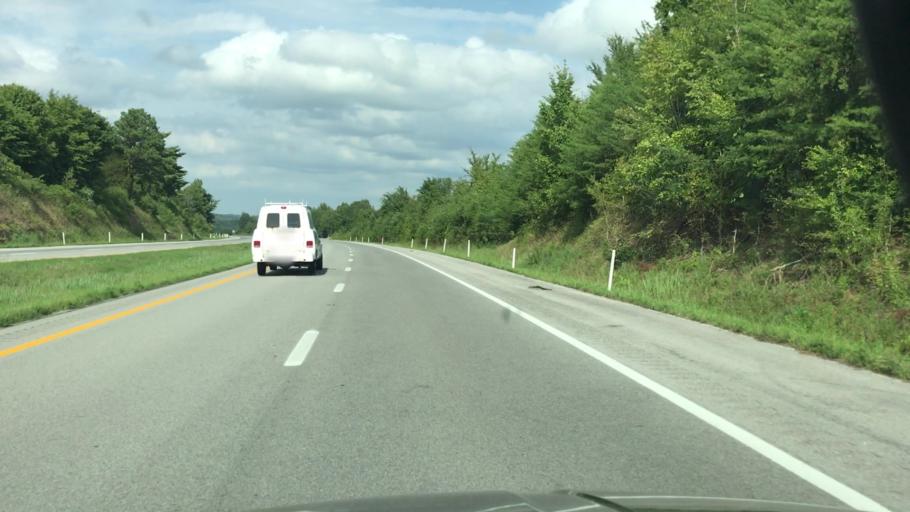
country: US
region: Kentucky
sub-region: Hopkins County
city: Dawson Springs
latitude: 37.1711
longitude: -87.7411
